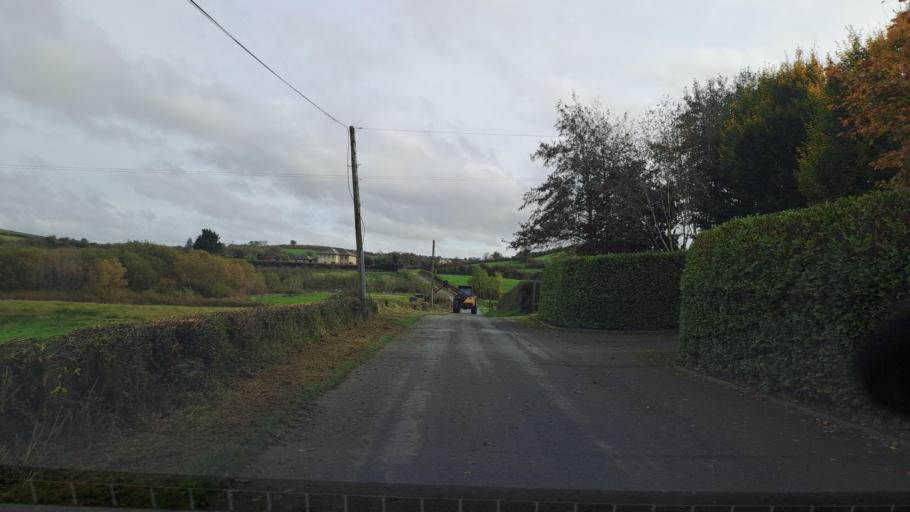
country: IE
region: Ulster
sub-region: An Cabhan
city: Bailieborough
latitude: 54.0208
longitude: -6.9130
